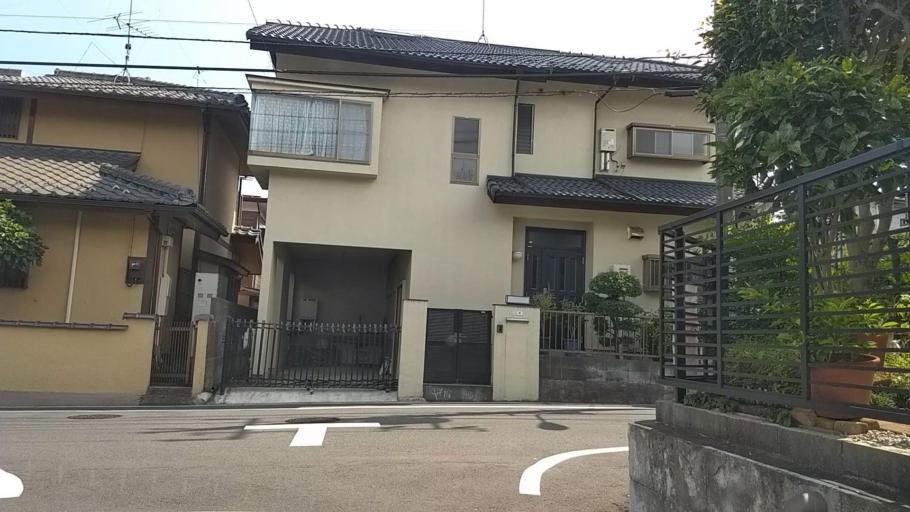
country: JP
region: Tokyo
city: Hachioji
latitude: 35.6498
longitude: 139.3154
